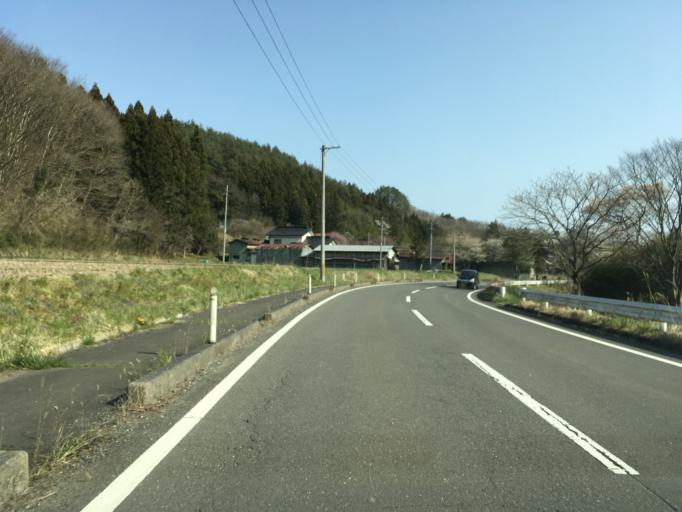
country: JP
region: Iwate
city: Ichinoseki
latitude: 38.7961
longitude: 141.3199
